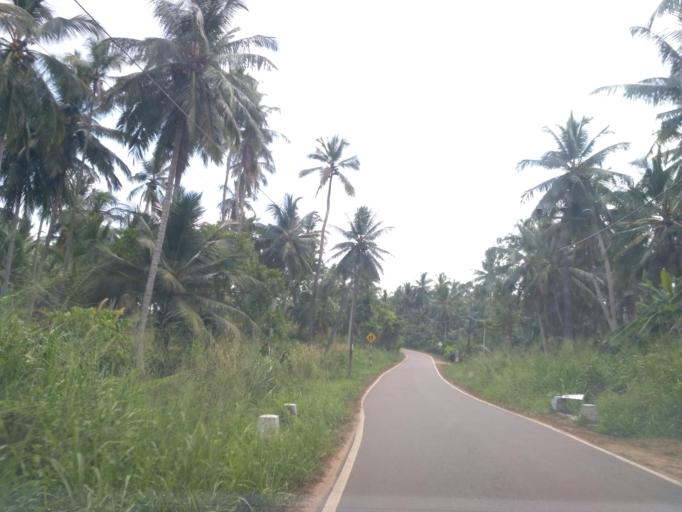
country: LK
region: North Western
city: Kuliyapitiya
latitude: 7.3356
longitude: 80.0618
